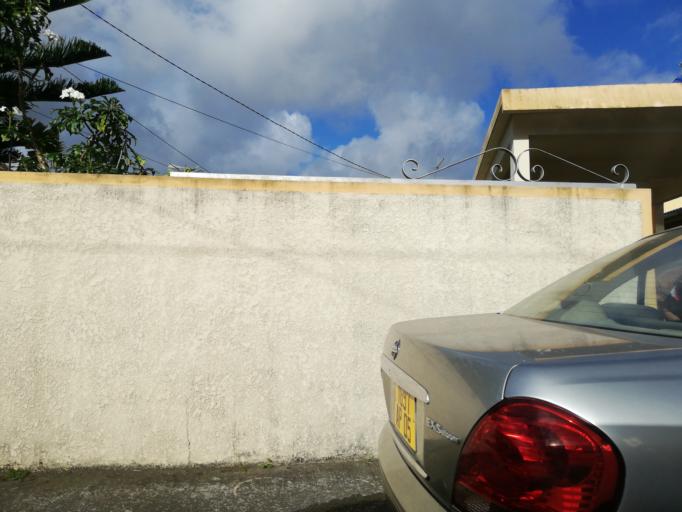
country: MU
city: Montagne Blanche
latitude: -20.2789
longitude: 57.6620
